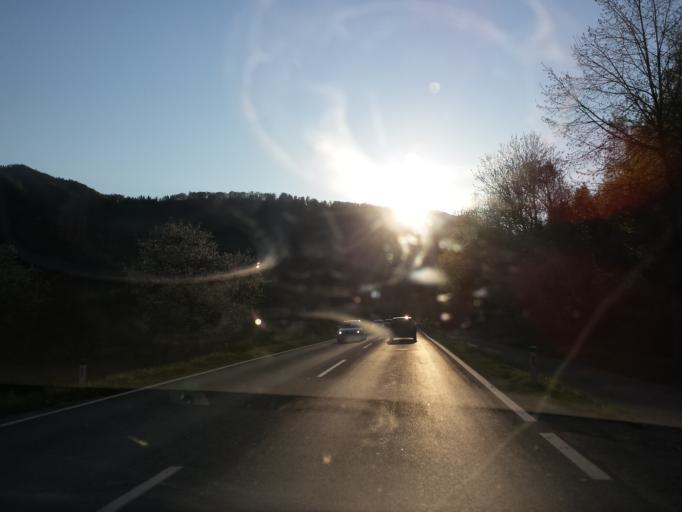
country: AT
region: Styria
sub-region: Graz Stadt
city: Goesting
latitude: 47.1105
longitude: 15.3851
